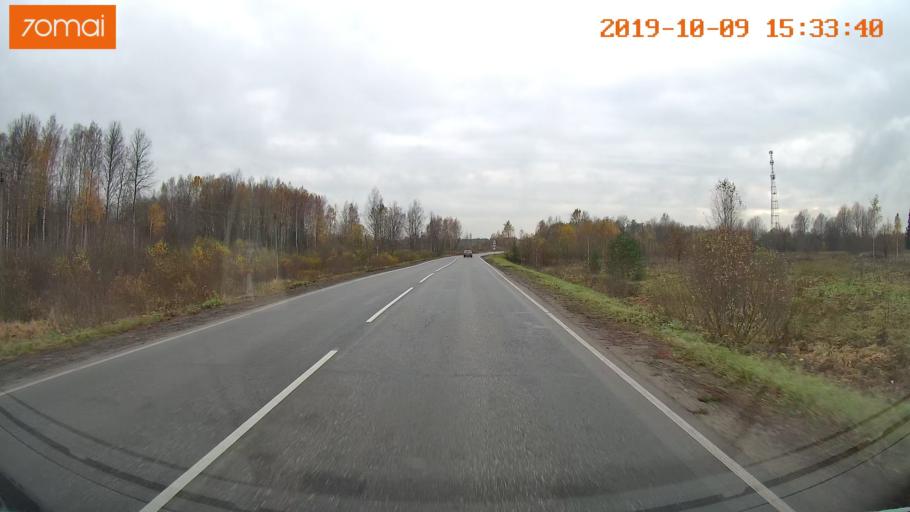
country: RU
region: Kostroma
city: Oktyabr'skiy
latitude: 57.9486
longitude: 41.2590
